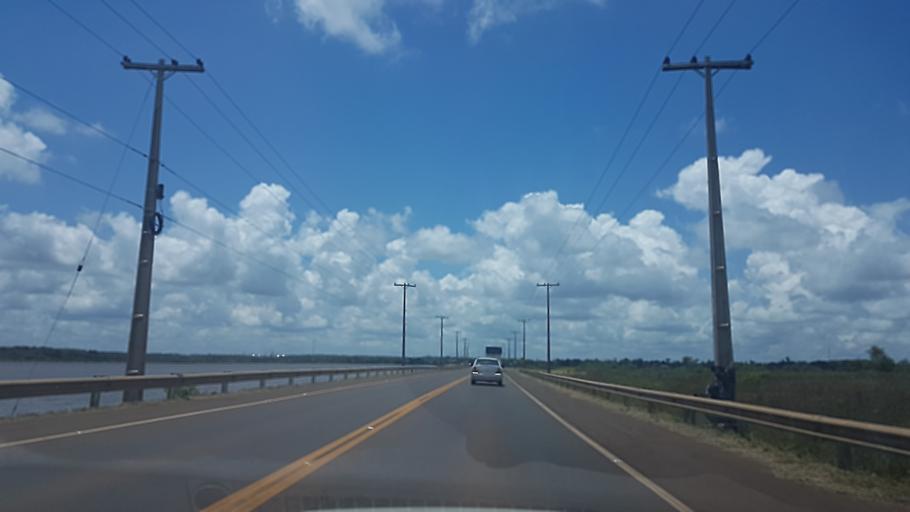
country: PY
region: Itapua
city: Carmen del Parana
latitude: -27.2091
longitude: -56.1617
